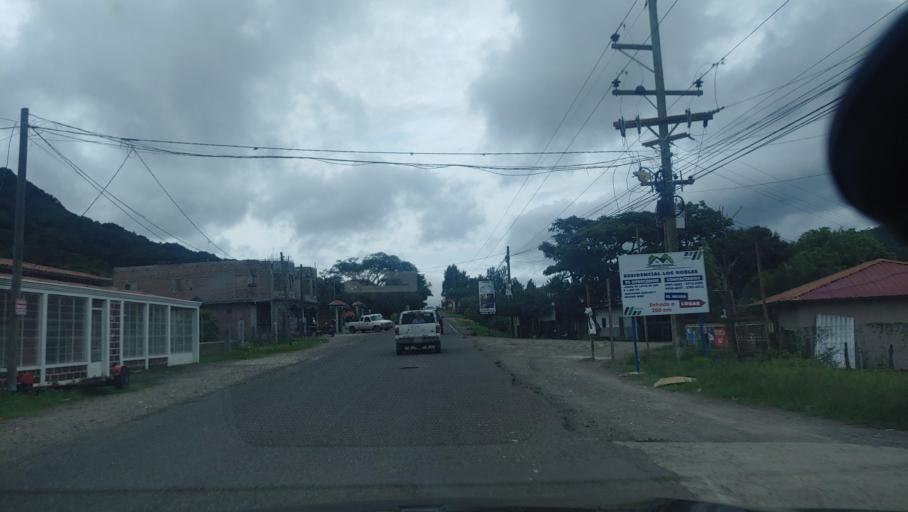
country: HN
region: Choluteca
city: San Marcos de Colon
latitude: 13.3757
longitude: -86.8988
